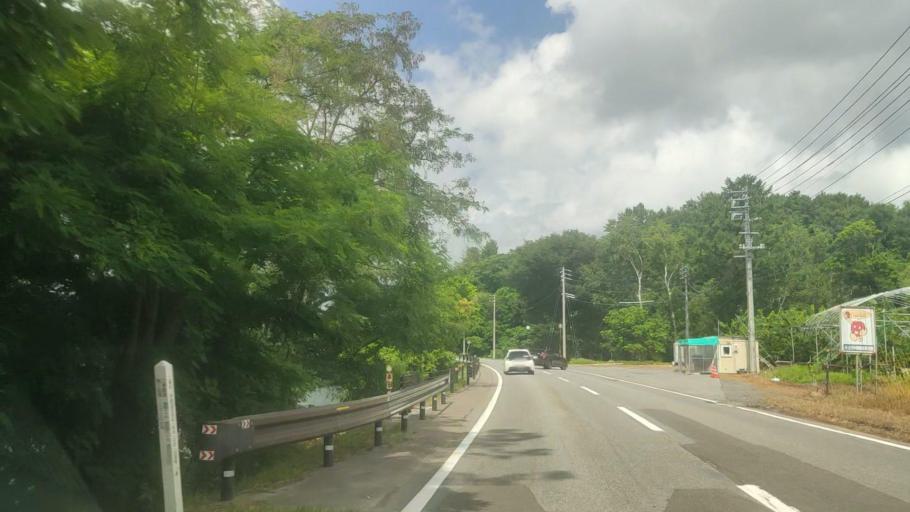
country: JP
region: Hokkaido
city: Date
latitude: 42.5598
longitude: 140.8776
